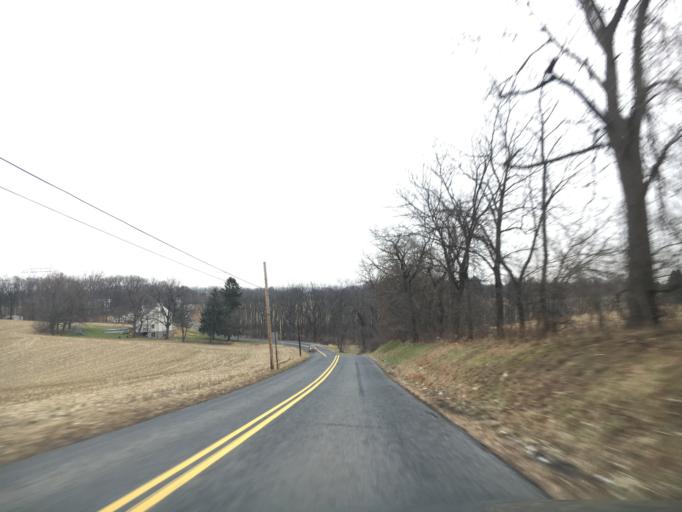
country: US
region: Pennsylvania
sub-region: Lehigh County
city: Egypt
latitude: 40.6858
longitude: -75.5671
